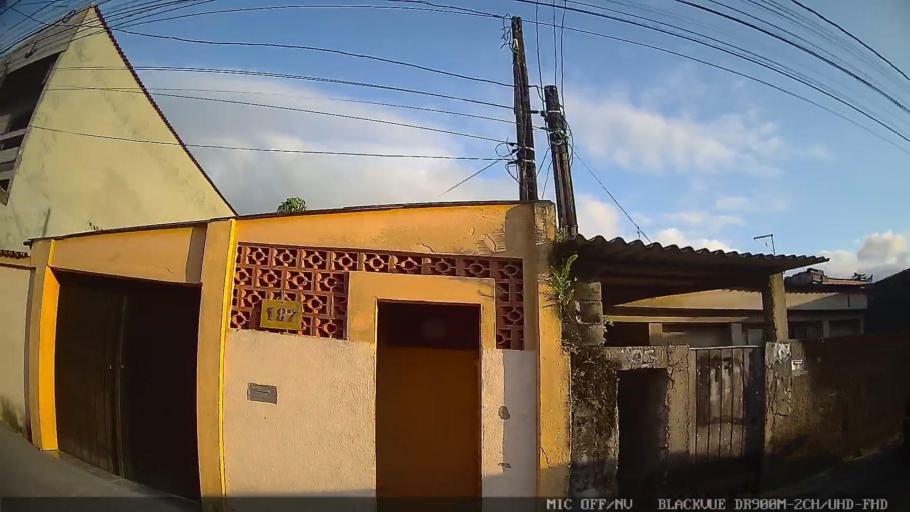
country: BR
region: Sao Paulo
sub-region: Itanhaem
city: Itanhaem
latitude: -24.1841
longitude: -46.8244
